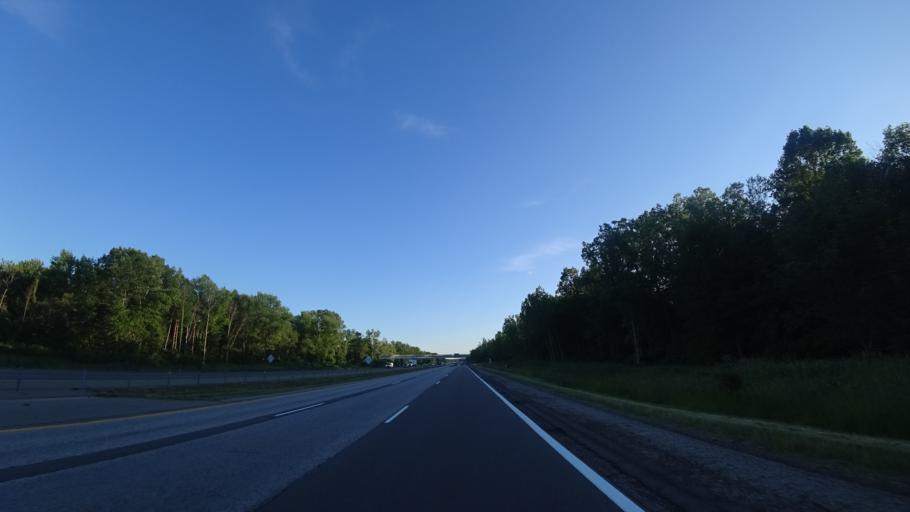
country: US
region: Michigan
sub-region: Berrien County
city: Shorewood-Tower Hills-Harbert
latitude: 41.9016
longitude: -86.5881
